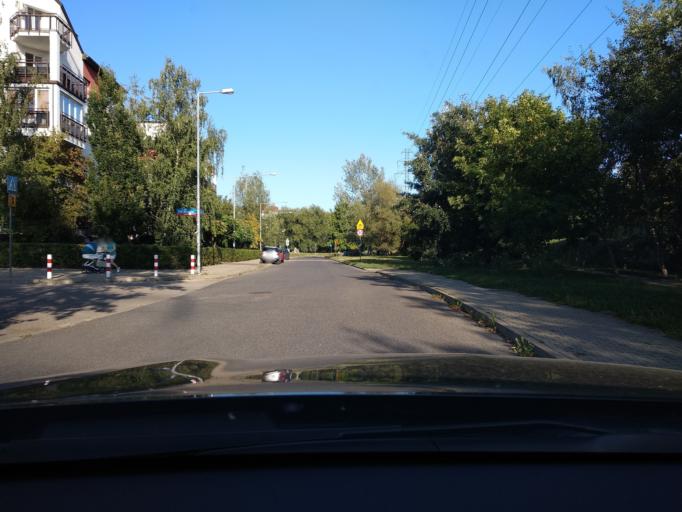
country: PL
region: Masovian Voivodeship
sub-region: Warszawa
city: Kabaty
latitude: 52.1277
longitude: 21.0587
